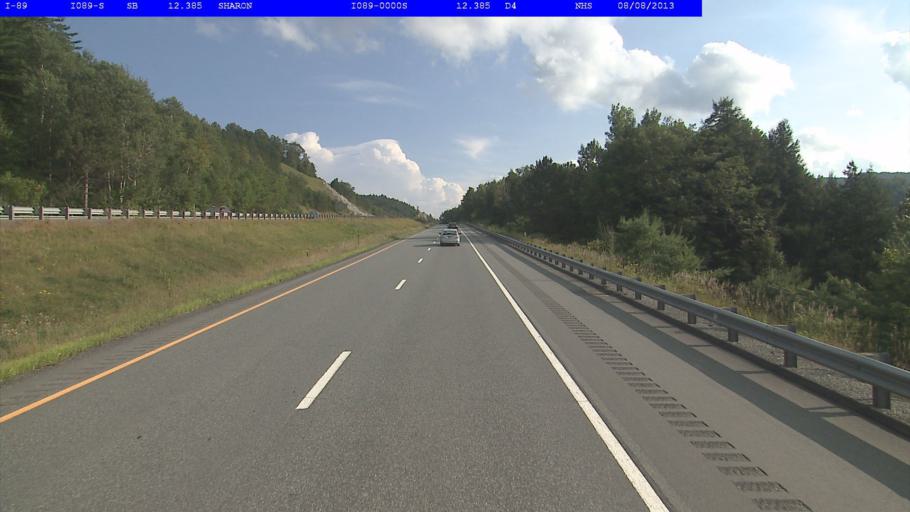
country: US
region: Vermont
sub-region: Windsor County
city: Woodstock
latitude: 43.7737
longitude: -72.4451
